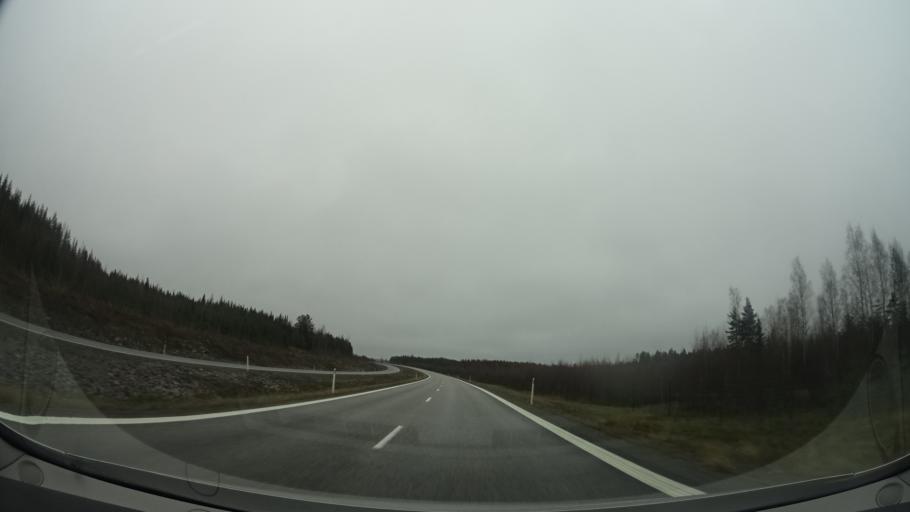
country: SE
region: Vaesterbotten
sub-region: Skelleftea Kommun
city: Kage
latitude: 64.8082
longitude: 21.0332
